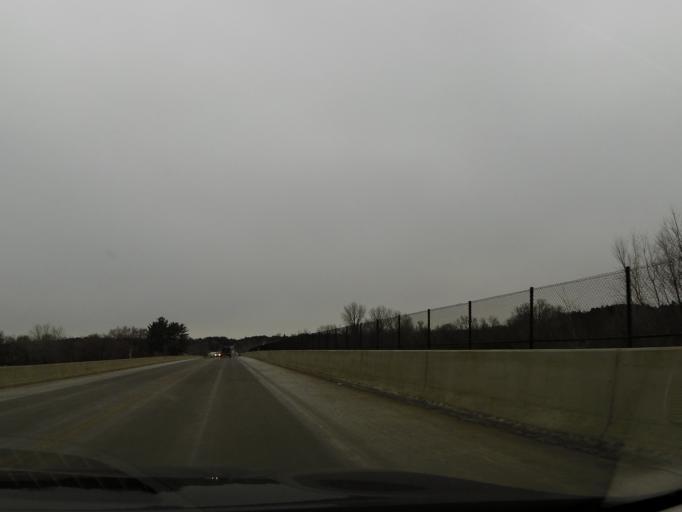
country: US
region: Minnesota
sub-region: Scott County
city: Jordan
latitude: 44.6938
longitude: -93.6428
